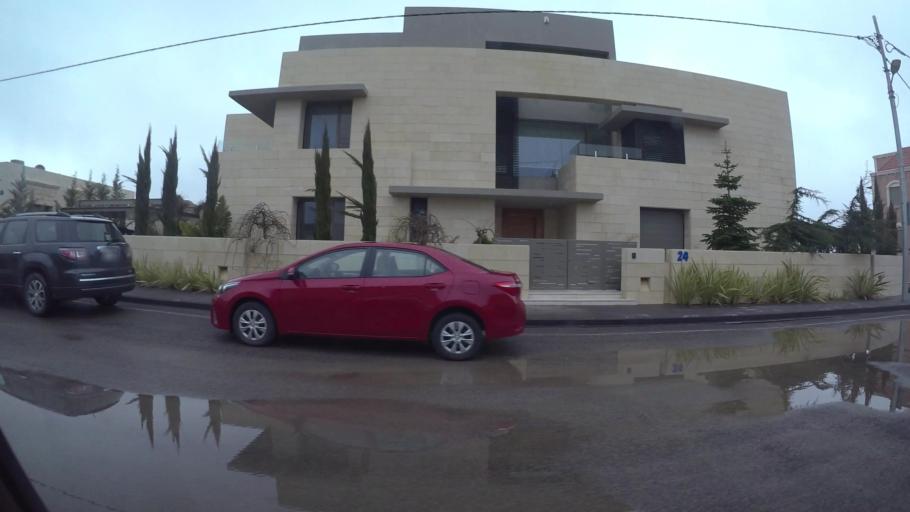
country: JO
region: Amman
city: Al Jubayhah
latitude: 32.0077
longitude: 35.8218
